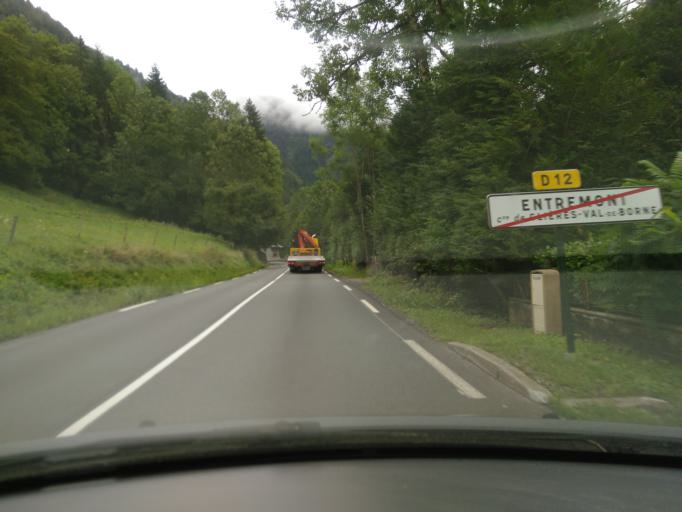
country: FR
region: Rhone-Alpes
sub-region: Departement de la Haute-Savoie
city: Saint-Jean-de-Sixt
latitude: 45.9509
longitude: 6.3941
